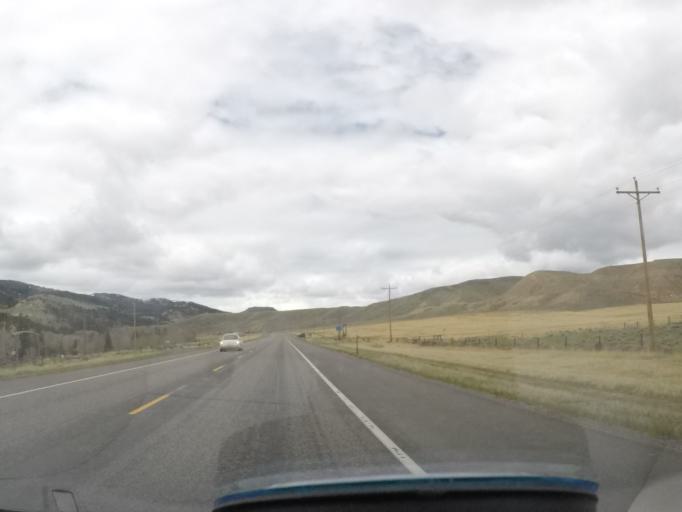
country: US
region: Wyoming
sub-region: Sublette County
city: Pinedale
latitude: 43.5766
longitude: -109.7367
